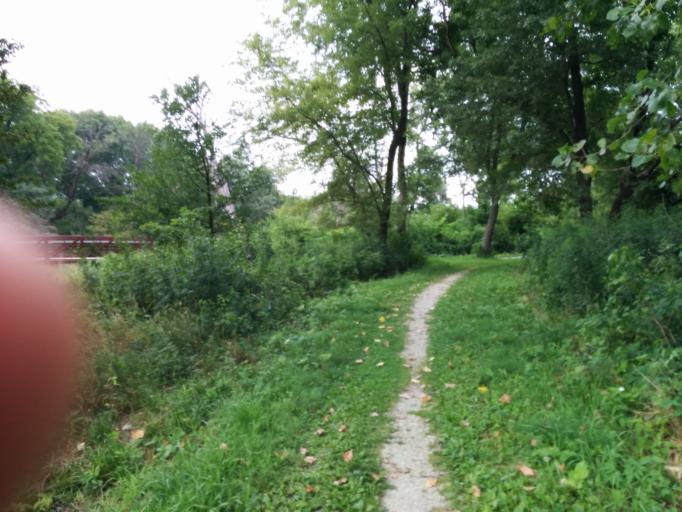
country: US
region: Illinois
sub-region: Cook County
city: Lyons
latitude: 41.8045
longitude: -87.8059
